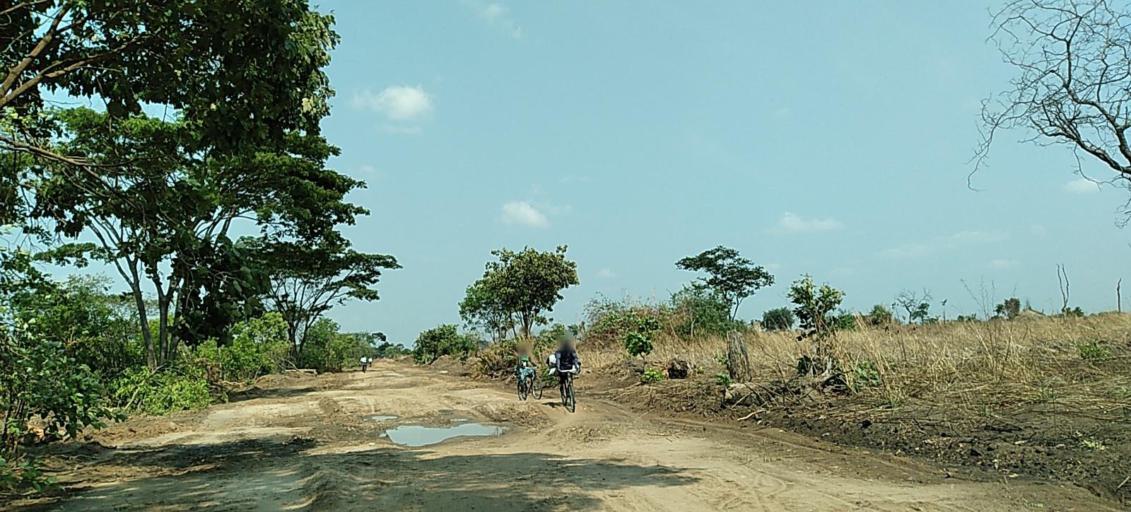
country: ZM
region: Copperbelt
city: Luanshya
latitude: -13.0897
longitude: 28.2681
